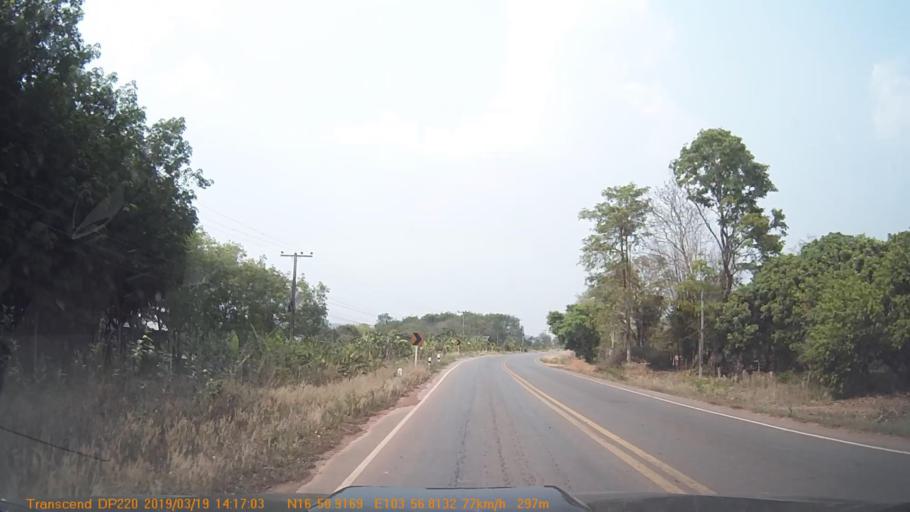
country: TH
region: Kalasin
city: Na Khu
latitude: 16.8490
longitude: 103.9469
